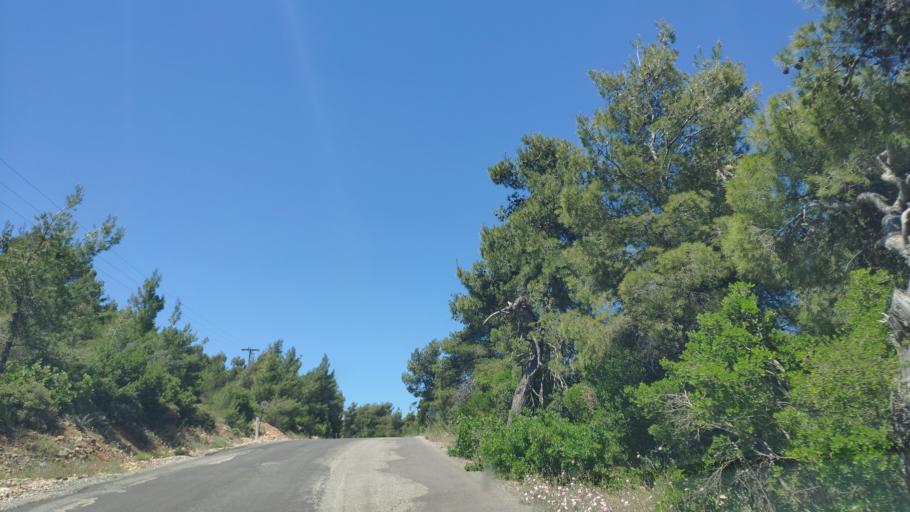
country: GR
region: Central Greece
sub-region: Nomos Voiotias
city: Kaparellion
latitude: 38.2044
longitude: 23.1632
